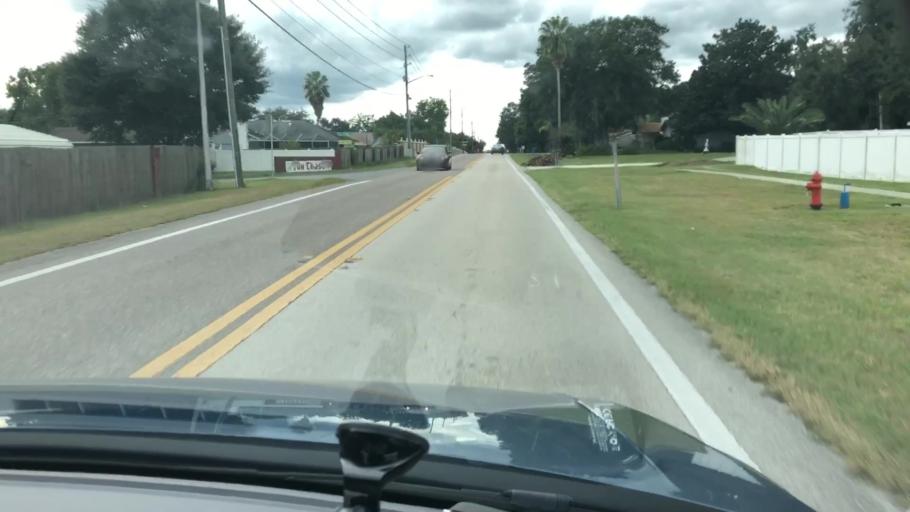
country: US
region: Florida
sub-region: Polk County
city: Kathleen
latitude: 28.1355
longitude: -82.0121
